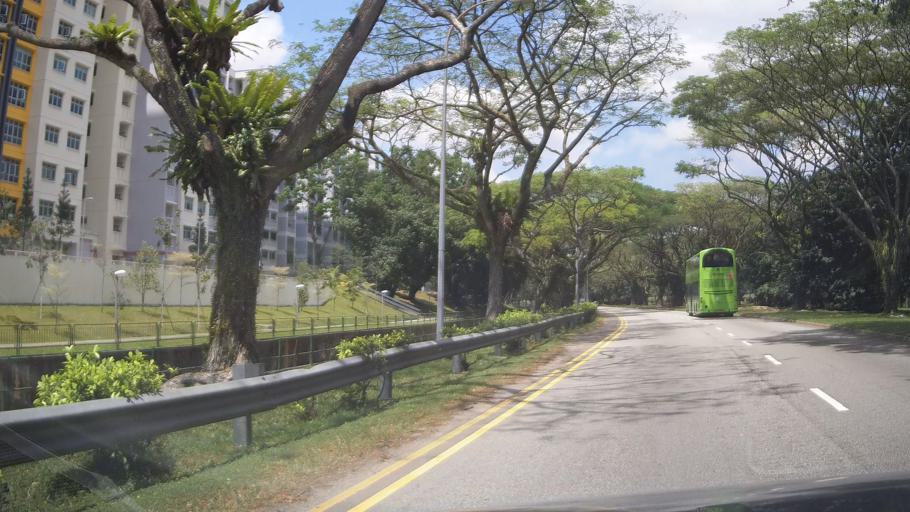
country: MY
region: Johor
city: Johor Bahru
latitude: 1.3553
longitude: 103.7201
